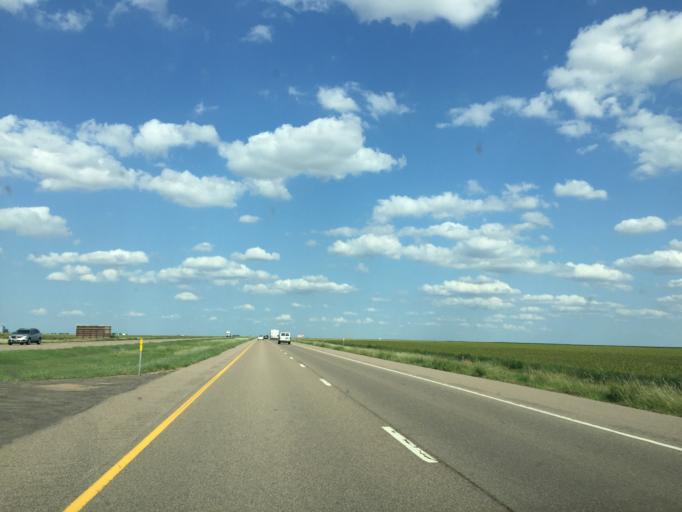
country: US
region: Kansas
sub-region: Gove County
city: Gove
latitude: 39.0970
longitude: -100.4041
